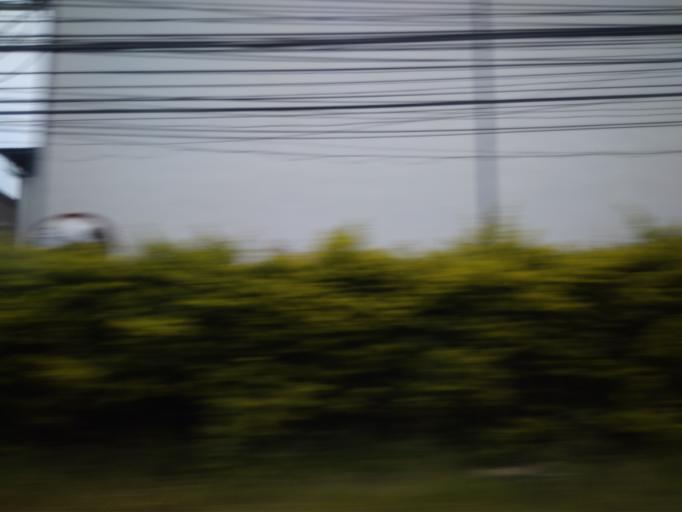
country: TH
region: Phuket
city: Mueang Phuket
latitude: 7.8269
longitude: 98.4018
